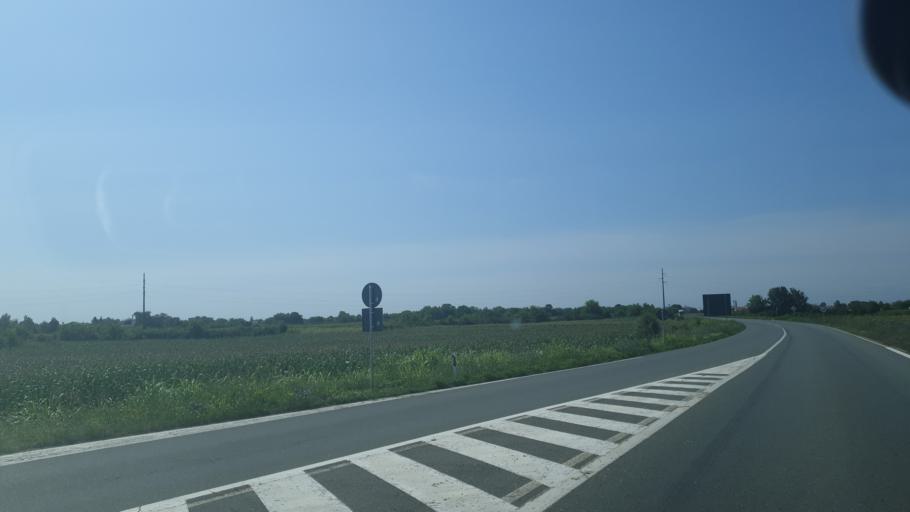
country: RS
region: Autonomna Pokrajina Vojvodina
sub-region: Sremski Okrug
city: Pecinci
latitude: 44.9164
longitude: 19.9569
